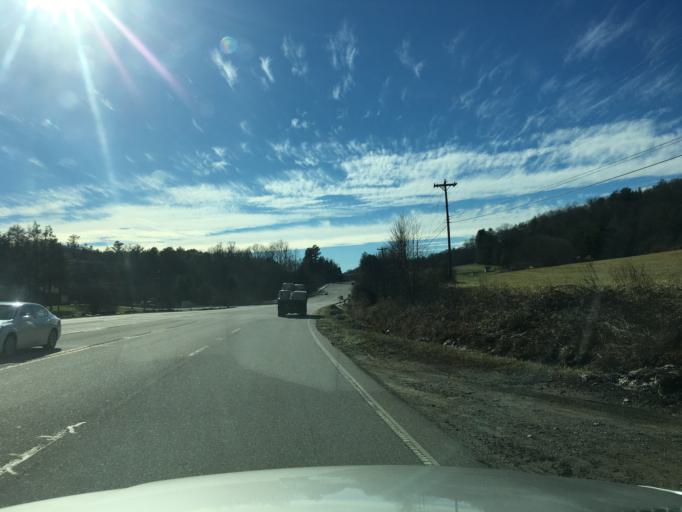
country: US
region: North Carolina
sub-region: Henderson County
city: Etowah
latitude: 35.3329
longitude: -82.6380
